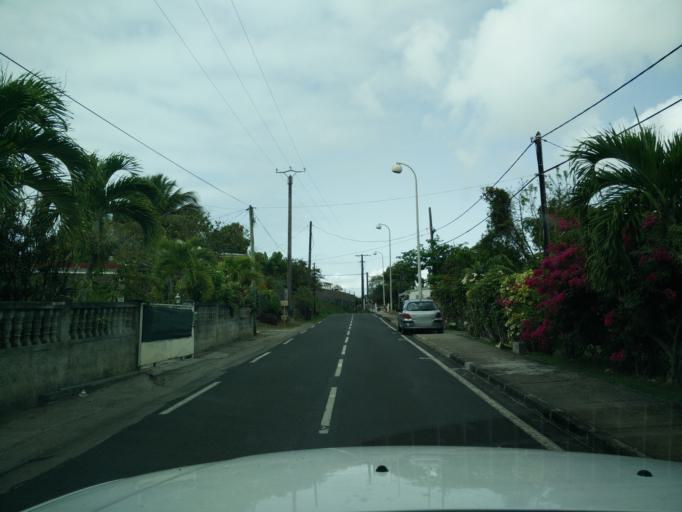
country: GP
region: Guadeloupe
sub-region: Guadeloupe
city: Le Gosier
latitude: 16.2175
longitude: -61.4595
